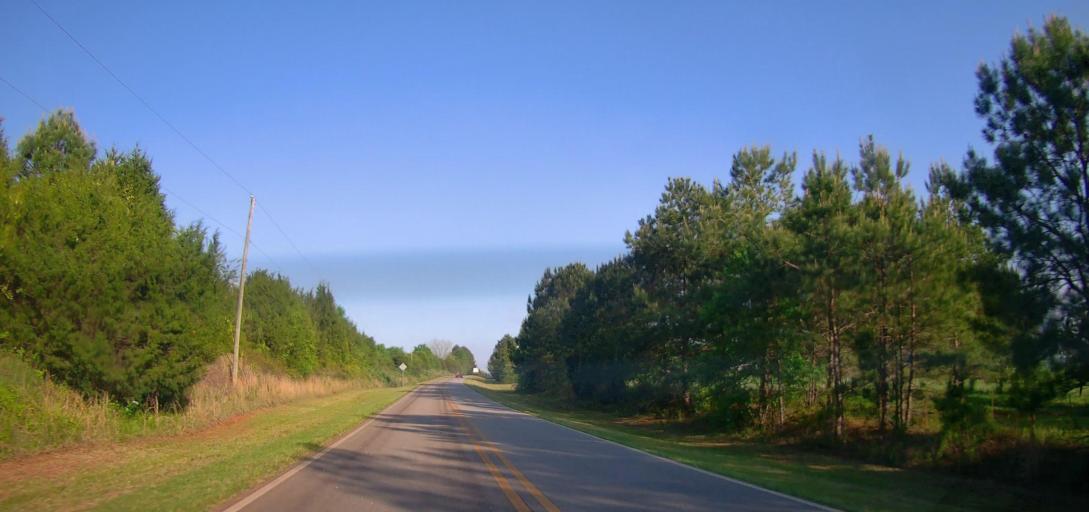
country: US
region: Georgia
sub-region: Putnam County
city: Eatonton
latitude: 33.3119
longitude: -83.3588
